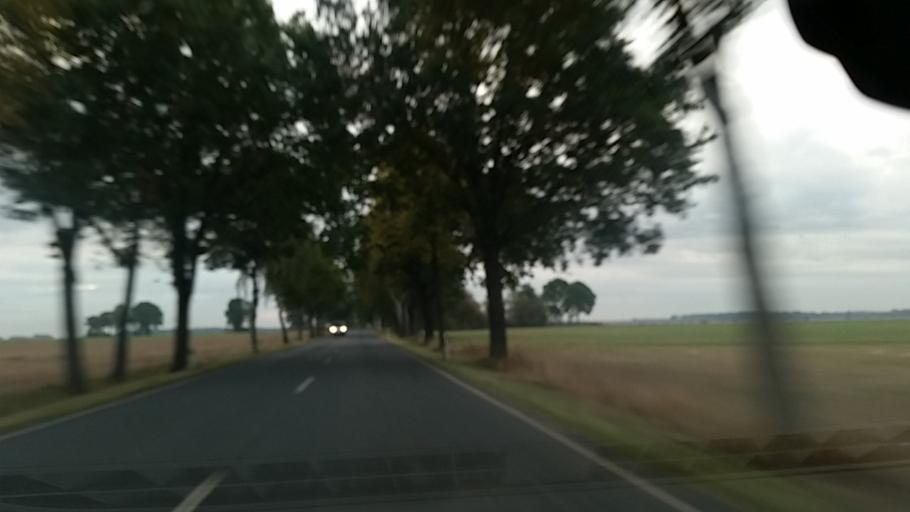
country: DE
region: Lower Saxony
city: Hankensbuttel
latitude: 52.7430
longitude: 10.5647
